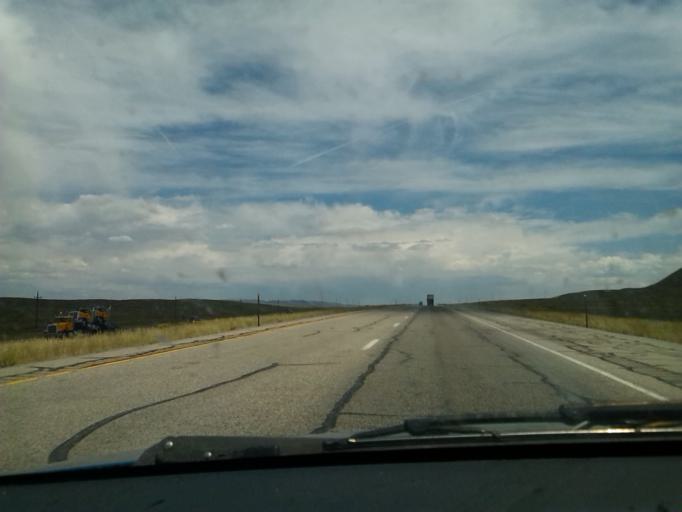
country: US
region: Wyoming
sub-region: Carbon County
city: Saratoga
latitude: 41.7432
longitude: -106.8856
